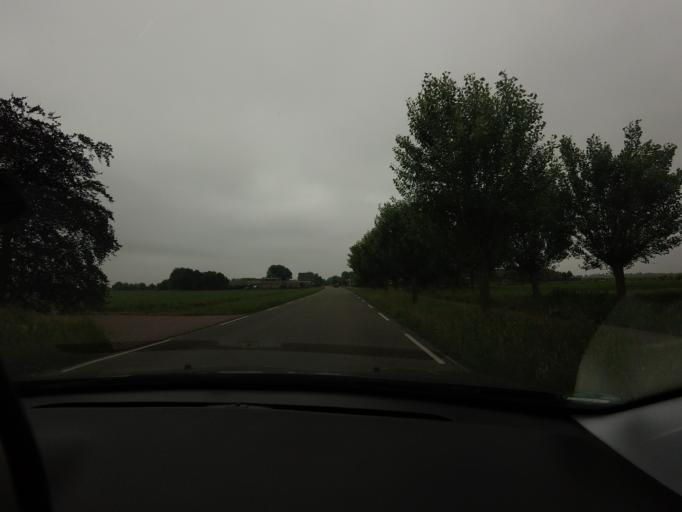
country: NL
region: Utrecht
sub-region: Gemeente Oudewater
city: Oudewater
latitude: 52.0549
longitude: 4.8117
